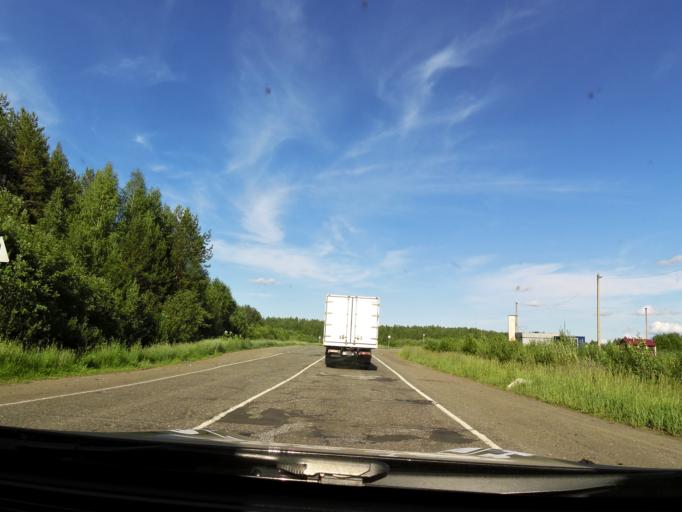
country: RU
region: Kirov
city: Dubrovka
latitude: 58.9039
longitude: 51.1990
